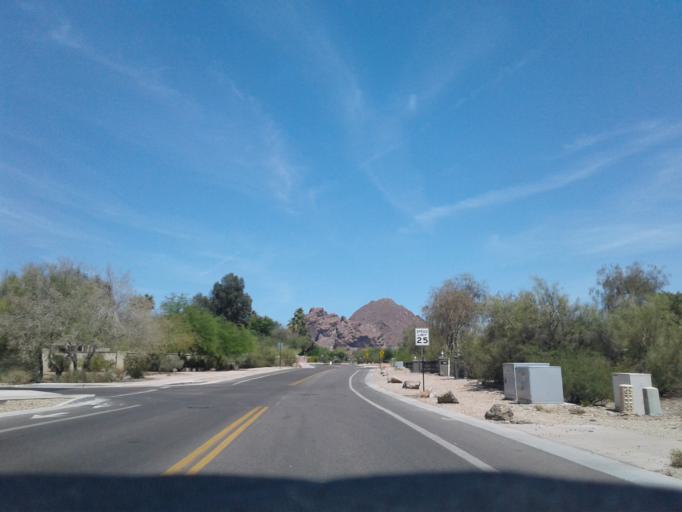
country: US
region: Arizona
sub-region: Maricopa County
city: Paradise Valley
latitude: 33.5173
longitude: -112.0071
